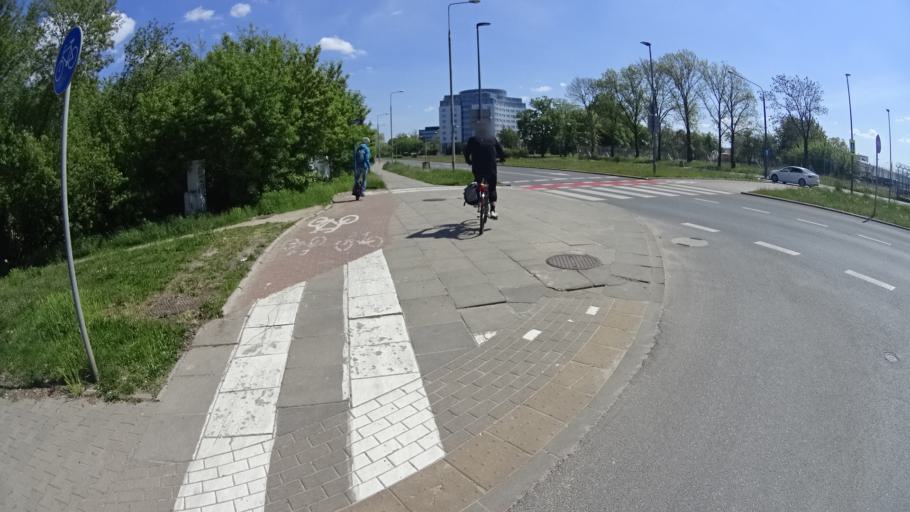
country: PL
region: Masovian Voivodeship
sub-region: Warszawa
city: Wlochy
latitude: 52.1847
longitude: 20.9604
